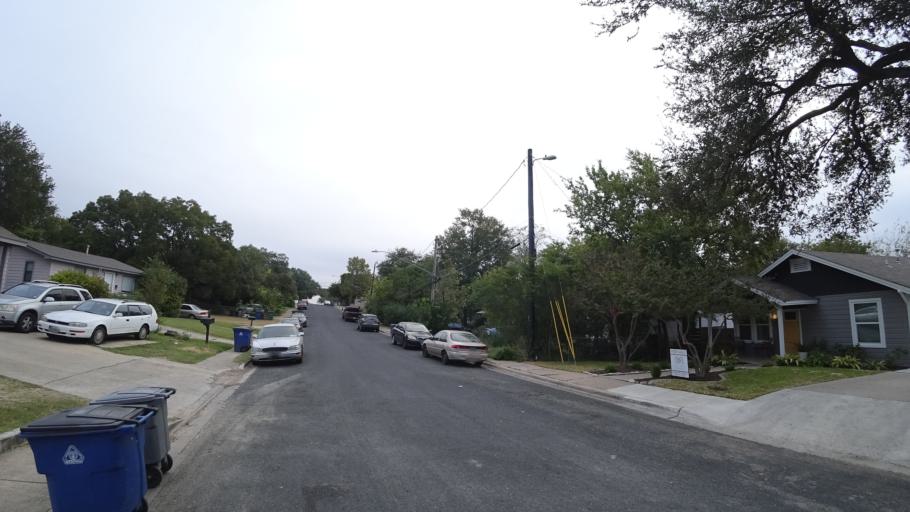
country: US
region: Texas
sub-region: Travis County
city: Austin
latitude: 30.2661
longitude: -97.7097
